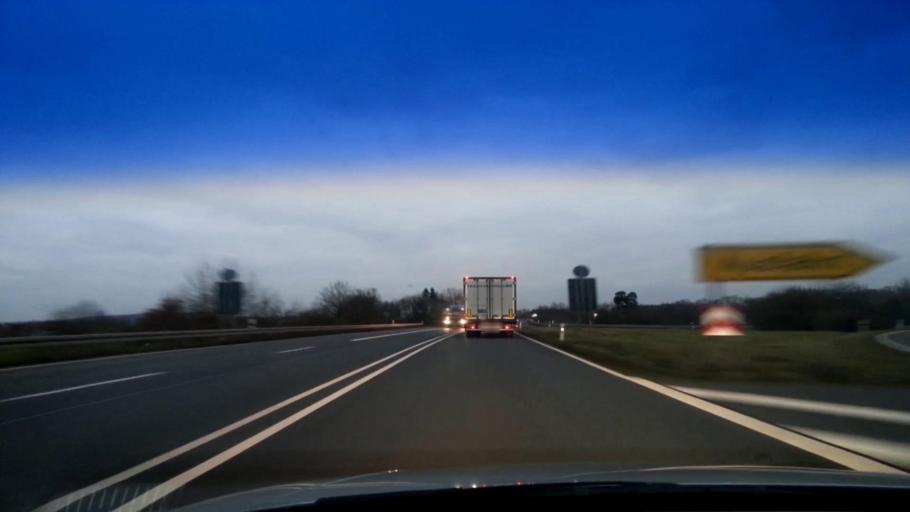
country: DE
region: Bavaria
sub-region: Upper Franconia
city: Pettstadt
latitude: 49.8280
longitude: 10.9516
